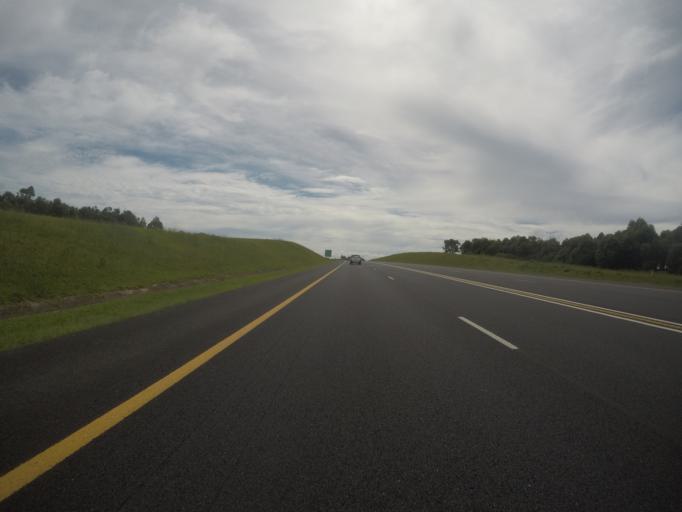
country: ZA
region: KwaZulu-Natal
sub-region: iLembe District Municipality
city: Mandeni
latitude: -29.0895
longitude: 31.6056
